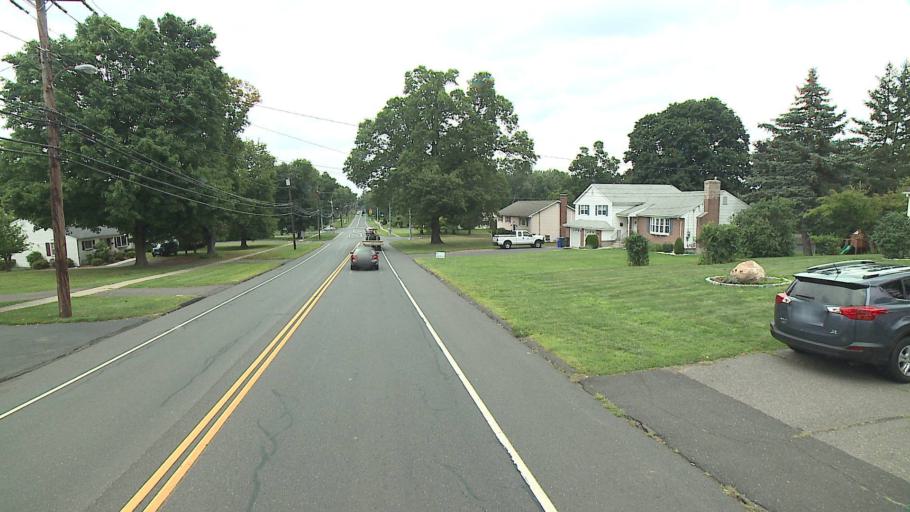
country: US
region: Connecticut
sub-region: Hartford County
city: Wethersfield
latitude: 41.6791
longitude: -72.6655
